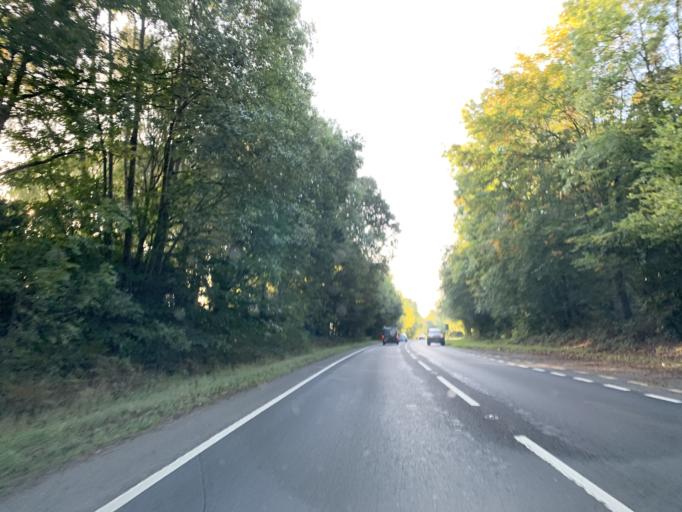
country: GB
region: England
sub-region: Wiltshire
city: Whiteparish
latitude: 50.9924
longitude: -1.6436
